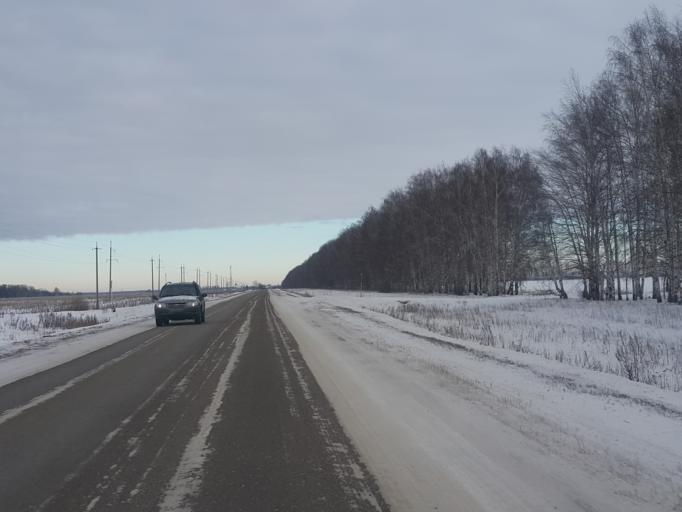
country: RU
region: Tambov
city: Novaya Lyada
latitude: 52.8104
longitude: 41.7900
